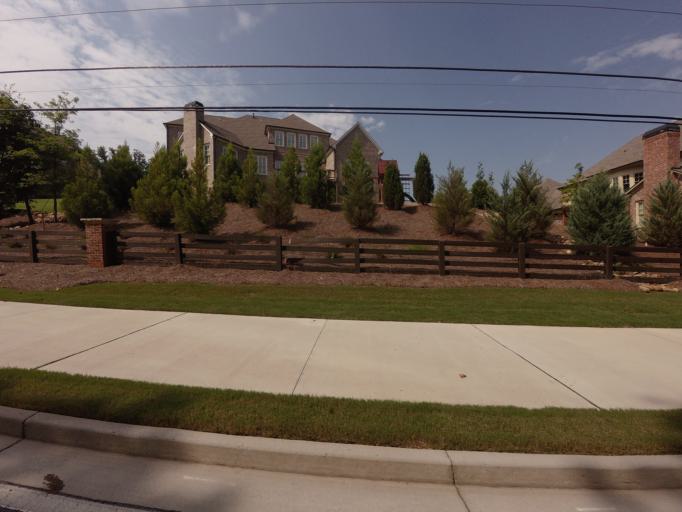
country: US
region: Georgia
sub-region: Fulton County
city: Johns Creek
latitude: 34.0302
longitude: -84.2307
